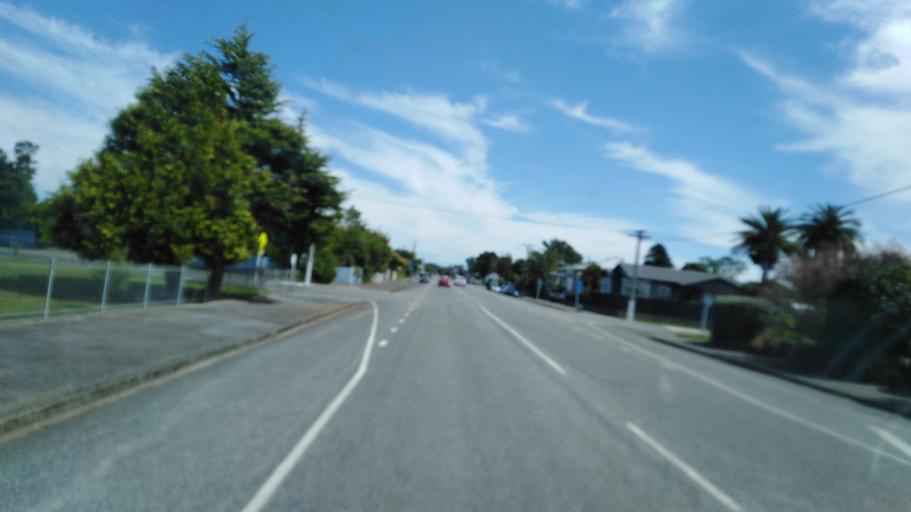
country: NZ
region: West Coast
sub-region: Buller District
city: Westport
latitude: -41.7546
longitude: 171.6051
